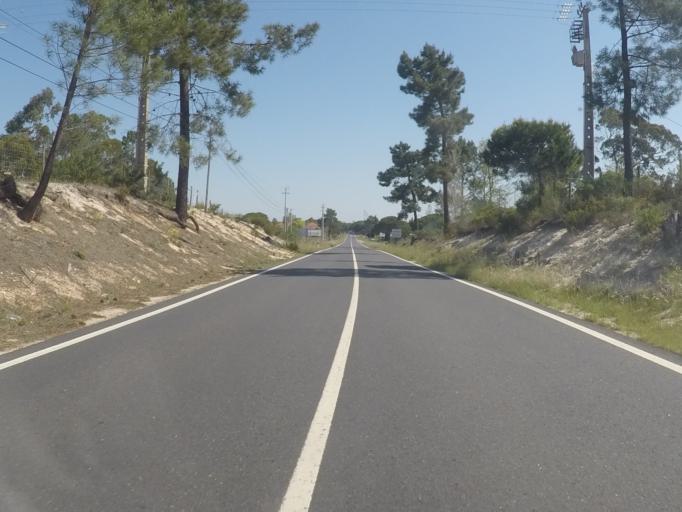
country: PT
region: Setubal
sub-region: Grandola
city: Grandola
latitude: 38.2634
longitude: -8.7302
